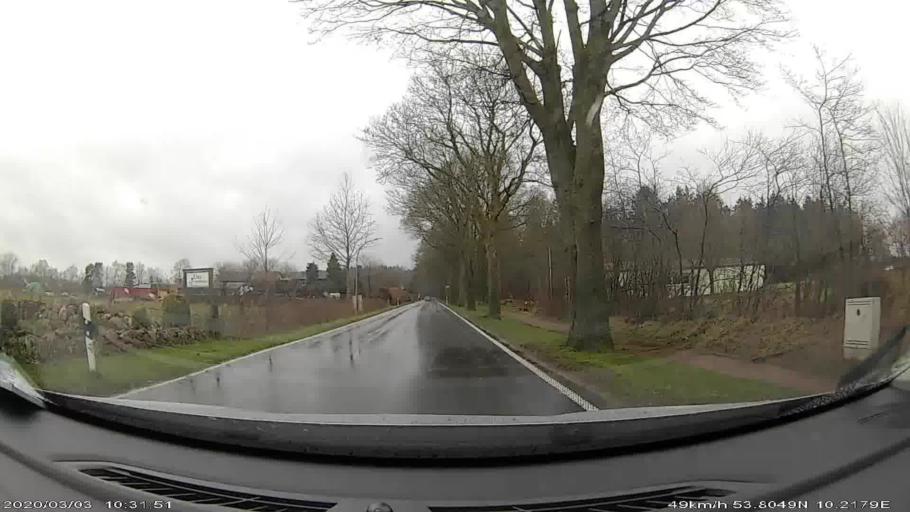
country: DE
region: Schleswig-Holstein
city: Sulfeld
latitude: 53.8062
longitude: 10.2134
